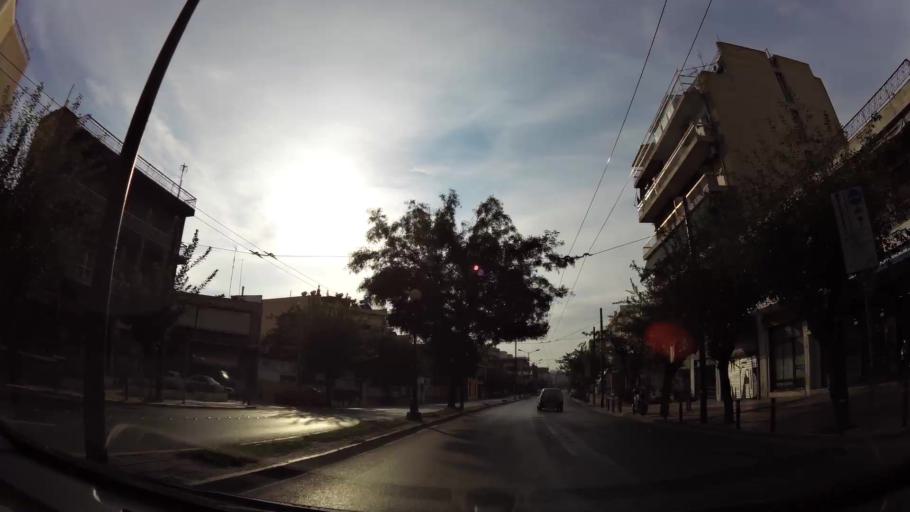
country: GR
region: Attica
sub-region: Nomarchia Athinas
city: Athens
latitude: 37.9958
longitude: 23.7121
